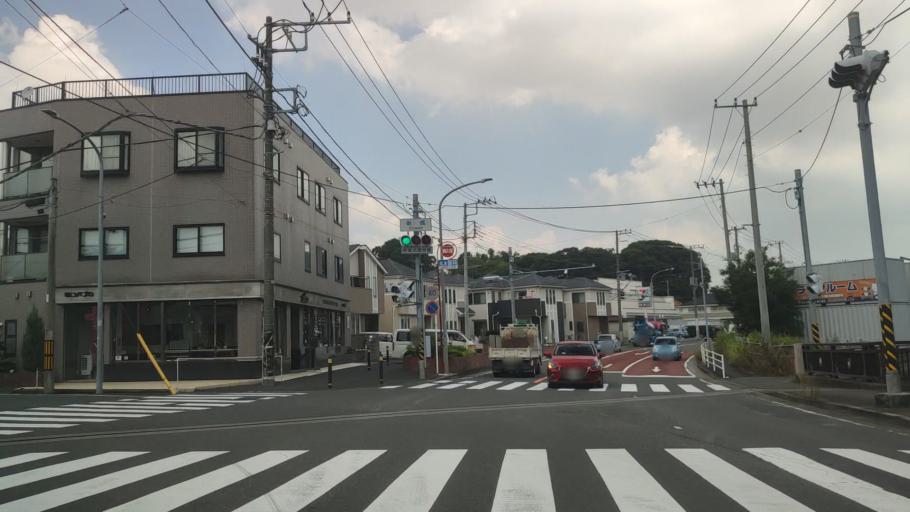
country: JP
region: Kanagawa
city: Minami-rinkan
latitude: 35.4322
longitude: 139.5127
